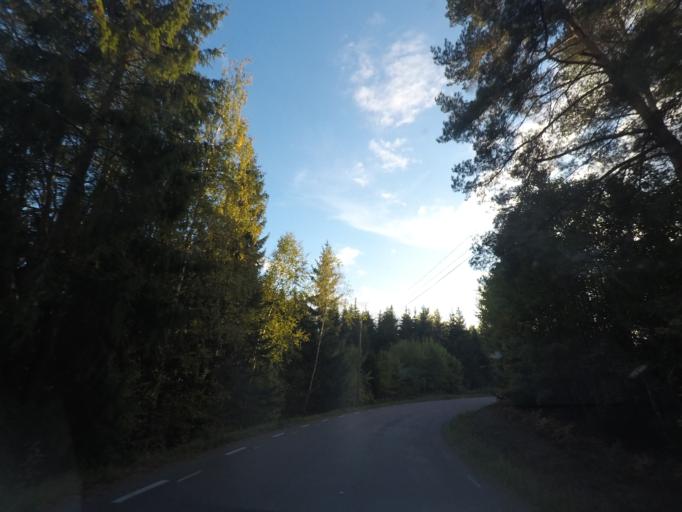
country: SE
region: Vaestmanland
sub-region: Kungsors Kommun
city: Kungsoer
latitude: 59.5070
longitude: 16.0962
